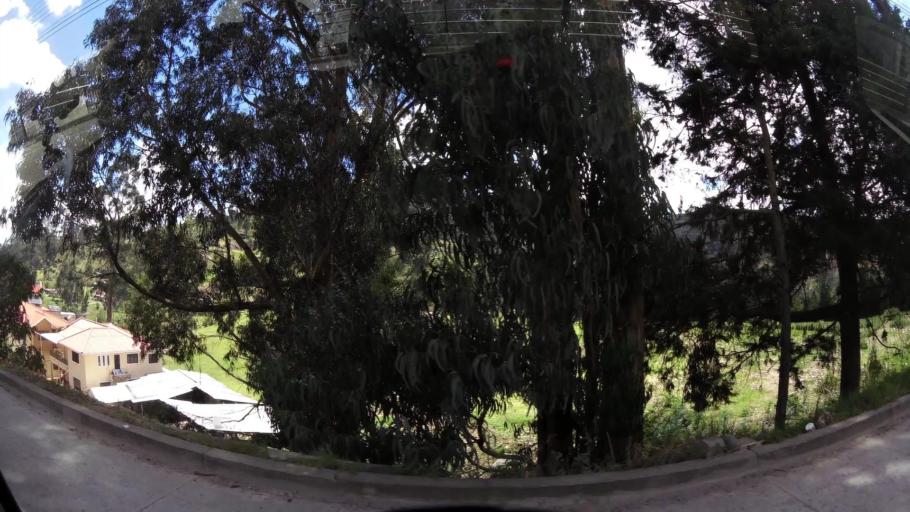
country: EC
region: Azuay
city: Cuenca
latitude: -2.9436
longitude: -79.0456
